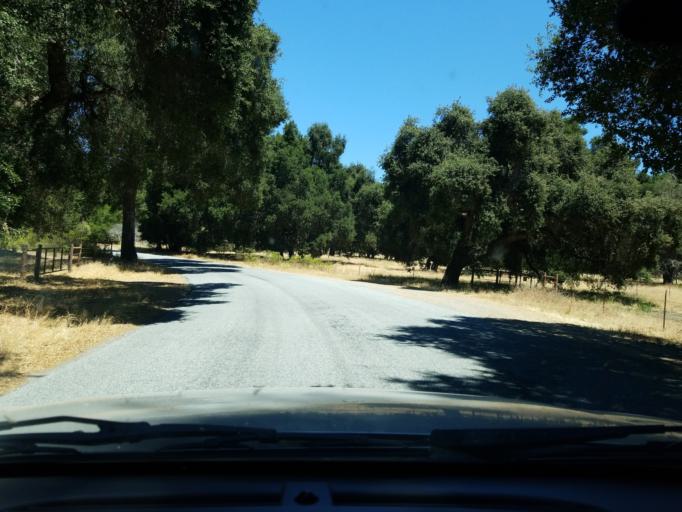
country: US
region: California
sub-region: Monterey County
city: Gonzales
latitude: 36.3921
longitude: -121.5676
